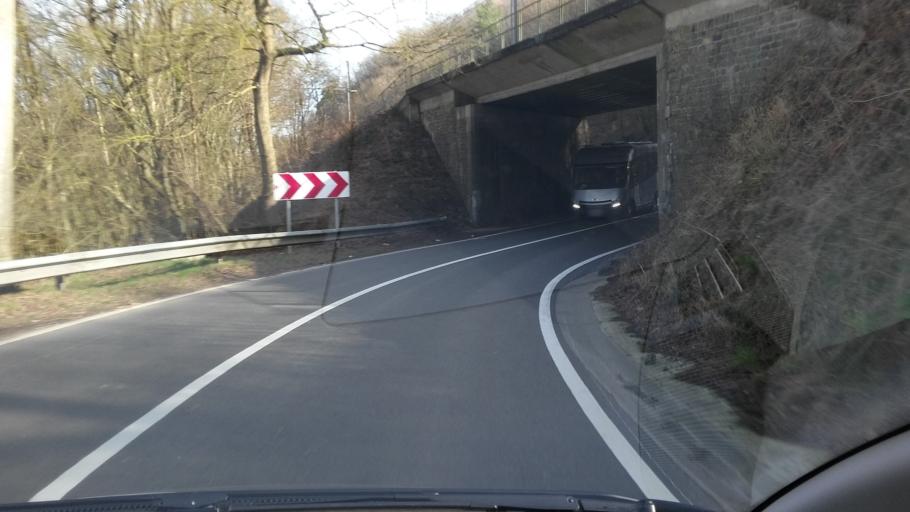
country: BE
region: Wallonia
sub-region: Province du Luxembourg
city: Durbuy
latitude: 50.3619
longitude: 5.5114
